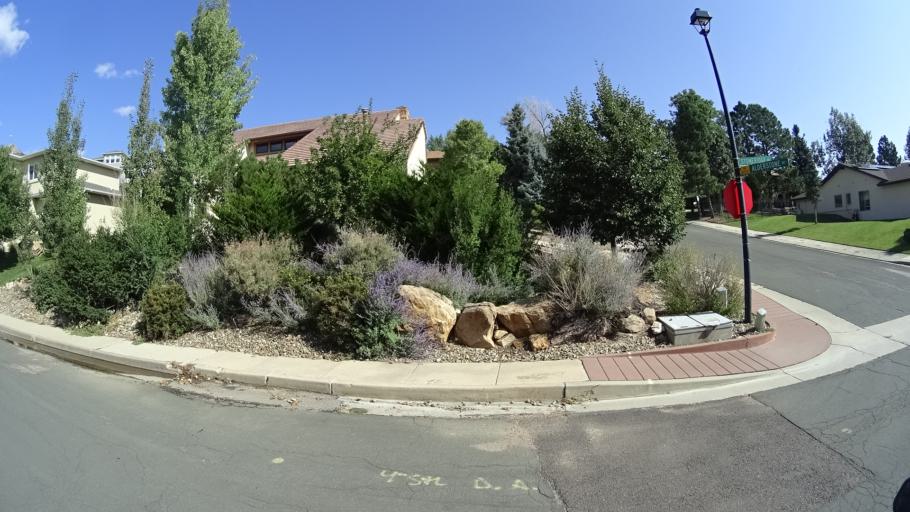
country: US
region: Colorado
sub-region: El Paso County
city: Manitou Springs
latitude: 38.9070
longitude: -104.8741
